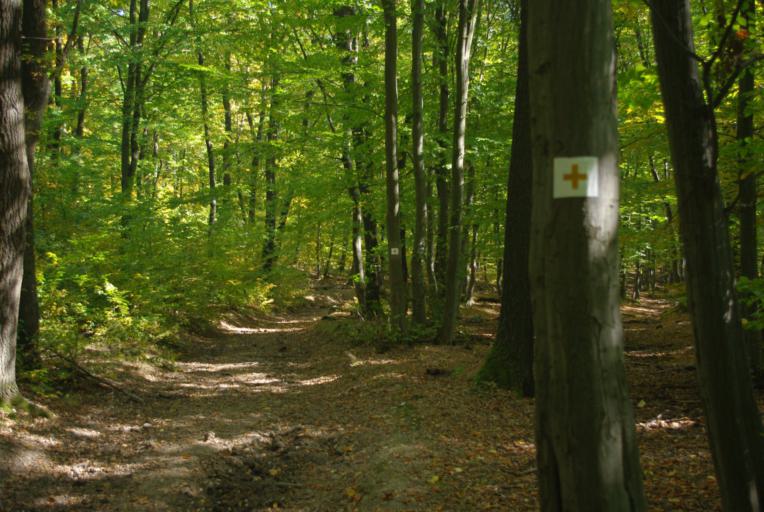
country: HU
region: Pest
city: Budakeszi
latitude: 47.5424
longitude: 18.8947
